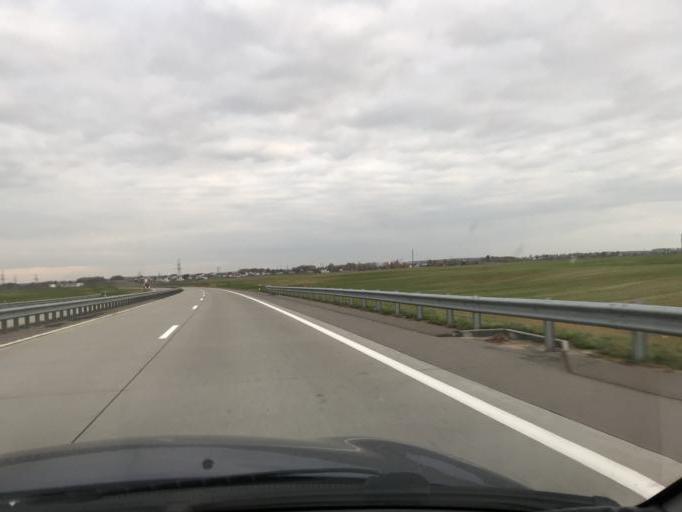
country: BY
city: Fanipol
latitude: 53.7648
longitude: 27.3738
